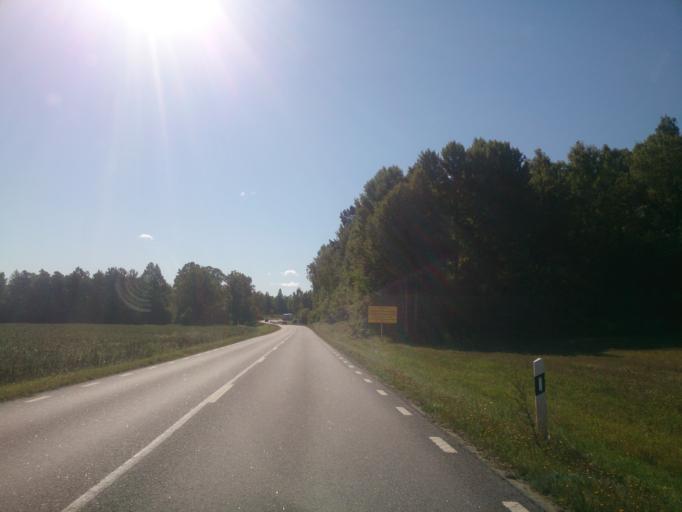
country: SE
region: OEstergoetland
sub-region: Atvidabergs Kommun
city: Atvidaberg
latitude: 58.2570
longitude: 15.9286
